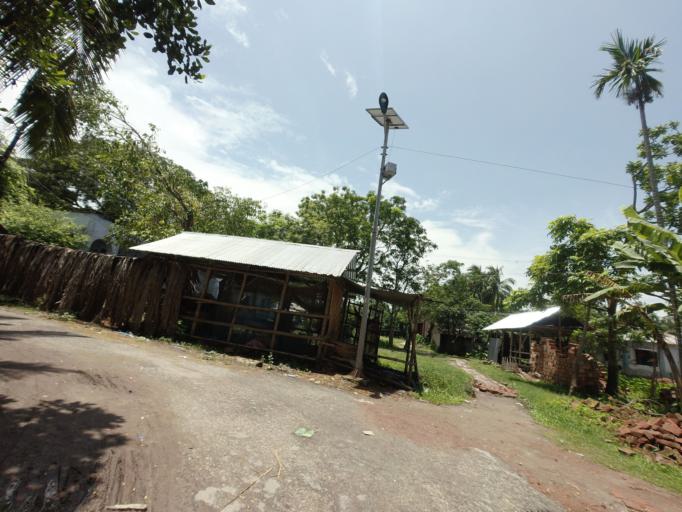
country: BD
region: Khulna
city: Kalia
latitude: 23.0438
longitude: 89.6316
